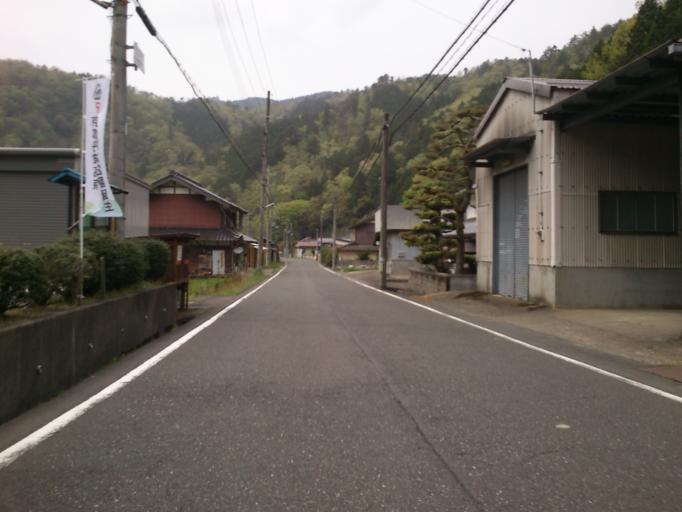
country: JP
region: Kyoto
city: Maizuru
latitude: 35.3852
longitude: 135.4594
